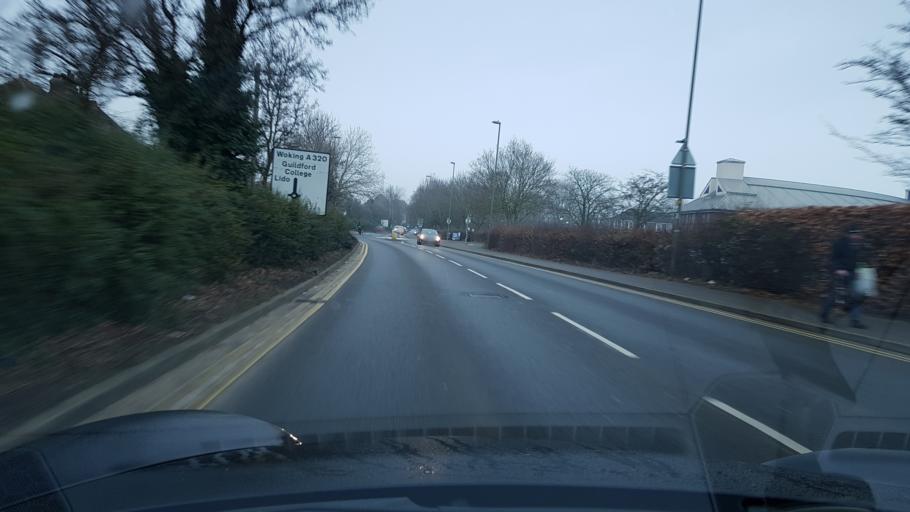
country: GB
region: England
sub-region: Surrey
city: Guildford
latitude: 51.2438
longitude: -0.5715
